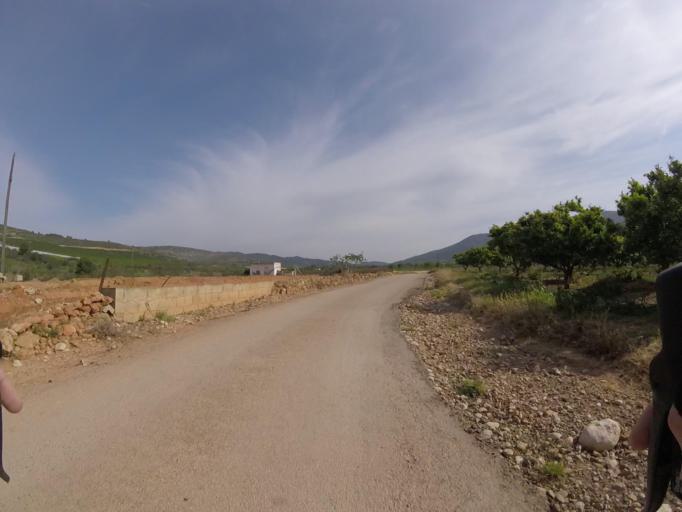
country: ES
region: Valencia
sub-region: Provincia de Castello
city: Alcala de Xivert
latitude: 40.2720
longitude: 0.2550
